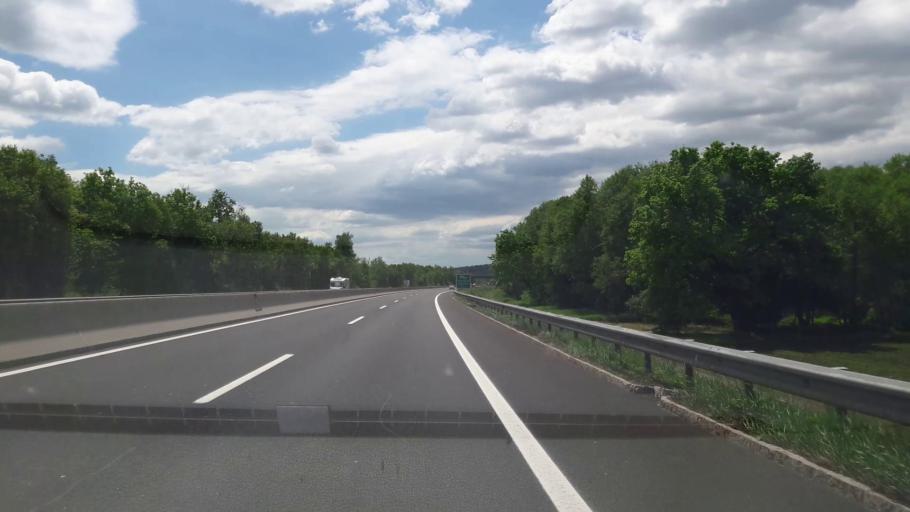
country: AT
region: Burgenland
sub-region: Politischer Bezirk Oberwart
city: Markt Allhau
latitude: 47.2957
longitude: 16.0701
